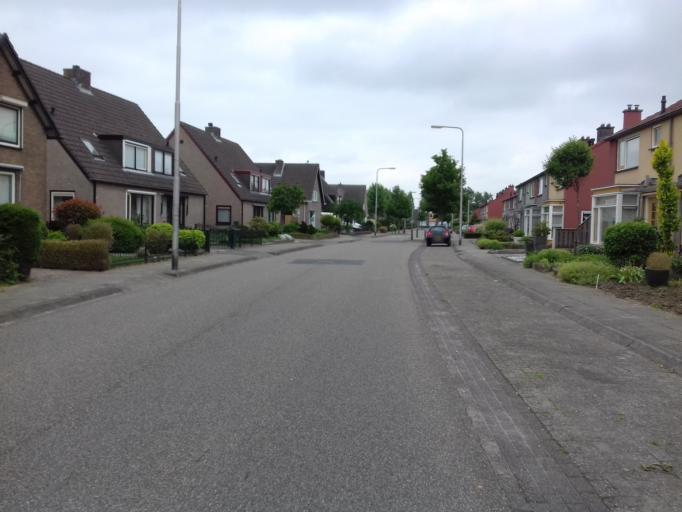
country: NL
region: Gelderland
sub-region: Gemeente Geldermalsen
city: Geldermalsen
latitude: 51.8840
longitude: 5.3013
